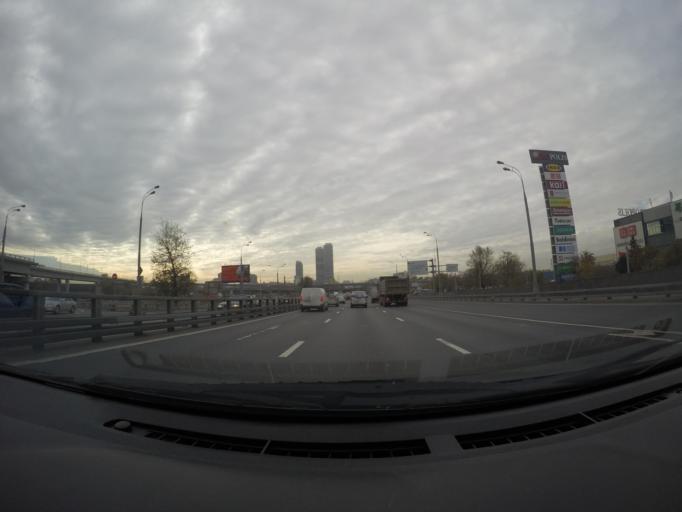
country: RU
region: Moscow
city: Rostokino
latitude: 55.8449
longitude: 37.6686
